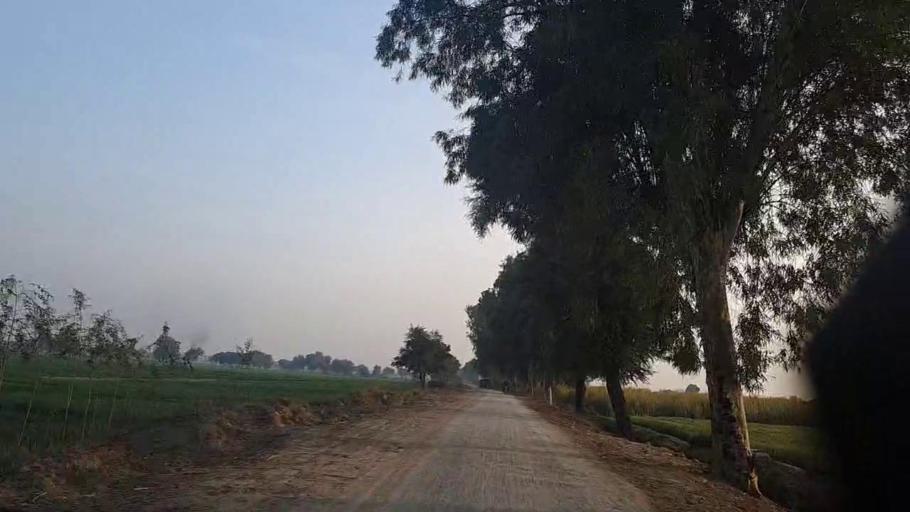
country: PK
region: Sindh
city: Sakrand
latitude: 26.1276
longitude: 68.2295
